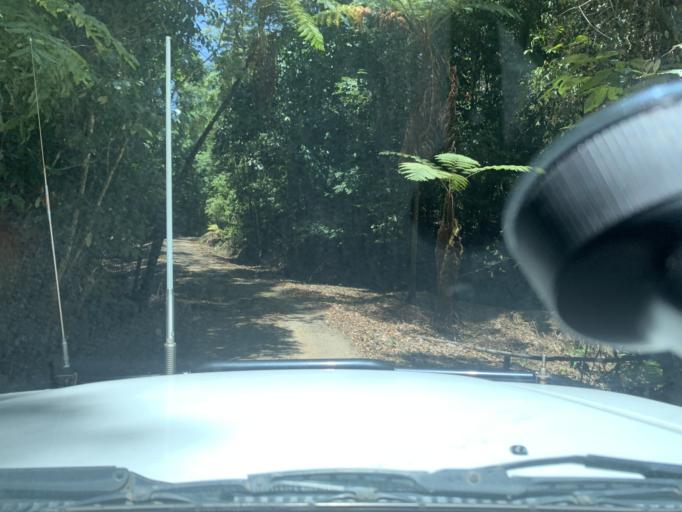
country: AU
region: Queensland
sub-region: Cairns
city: Redlynch
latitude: -16.9677
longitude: 145.6489
